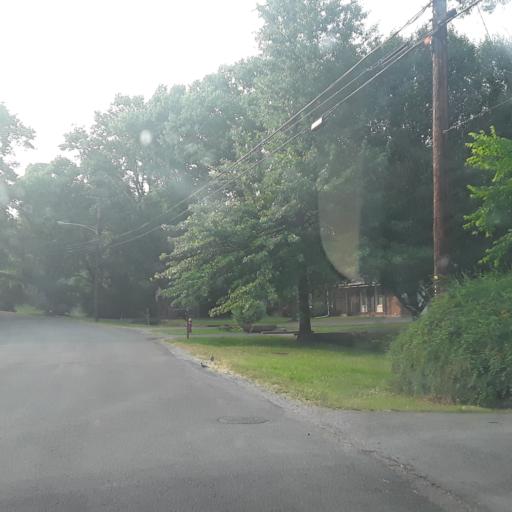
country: US
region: Tennessee
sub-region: Davidson County
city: Oak Hill
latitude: 36.0769
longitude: -86.7515
